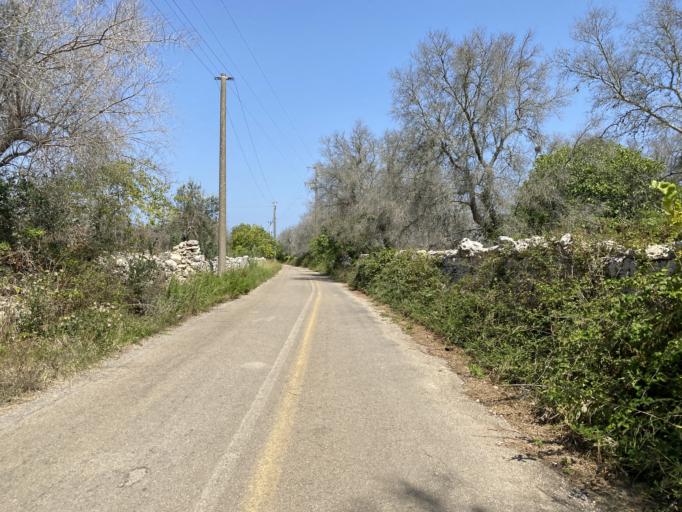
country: IT
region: Apulia
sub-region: Provincia di Lecce
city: Sanarica
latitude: 40.0974
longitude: 18.3539
